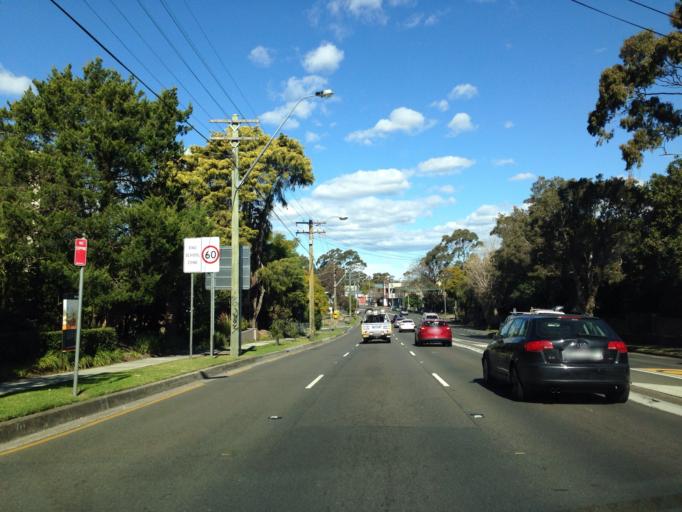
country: AU
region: New South Wales
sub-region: Ku-ring-gai
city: Killara
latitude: -33.7610
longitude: 151.1550
